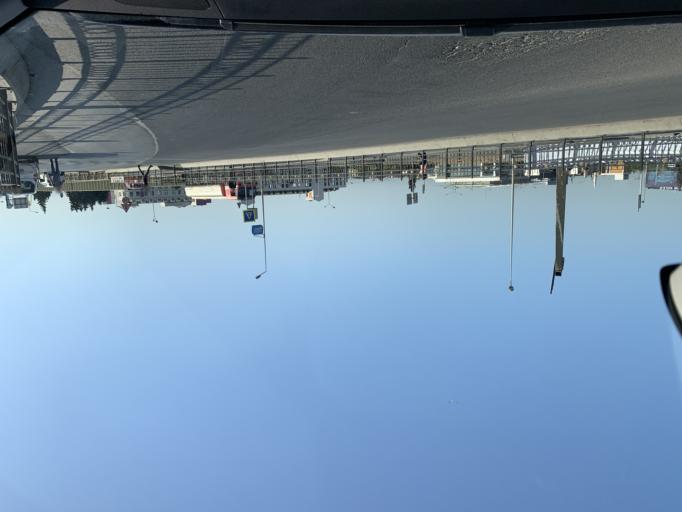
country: TR
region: Istanbul
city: Icmeler
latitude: 40.8501
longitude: 29.2986
